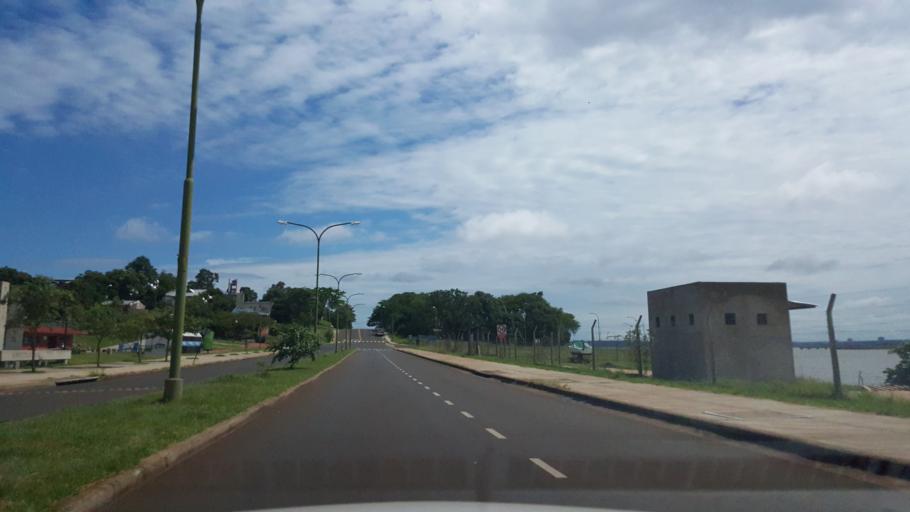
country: AR
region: Misiones
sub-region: Departamento de Capital
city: Posadas
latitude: -27.3574
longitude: -55.9114
